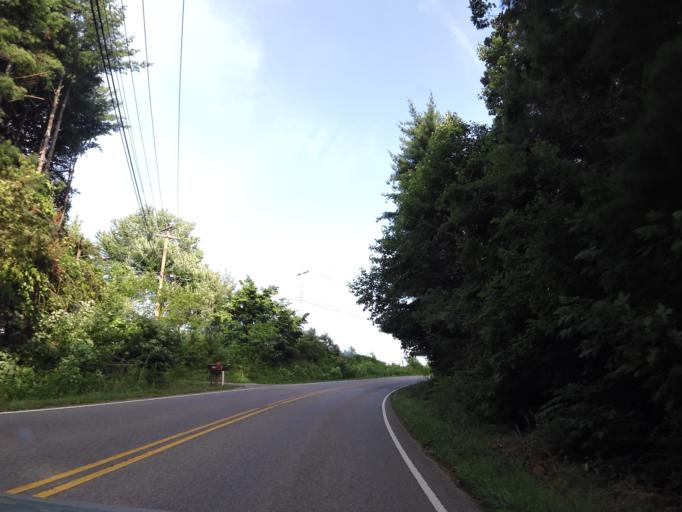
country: US
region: Tennessee
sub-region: Blount County
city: Eagleton Village
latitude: 35.8037
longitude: -83.9076
